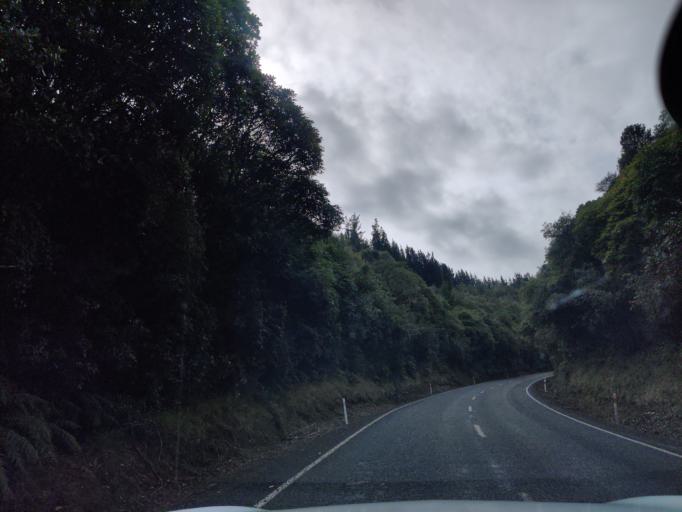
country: NZ
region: Waikato
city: Turangi
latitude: -38.7537
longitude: 175.6750
